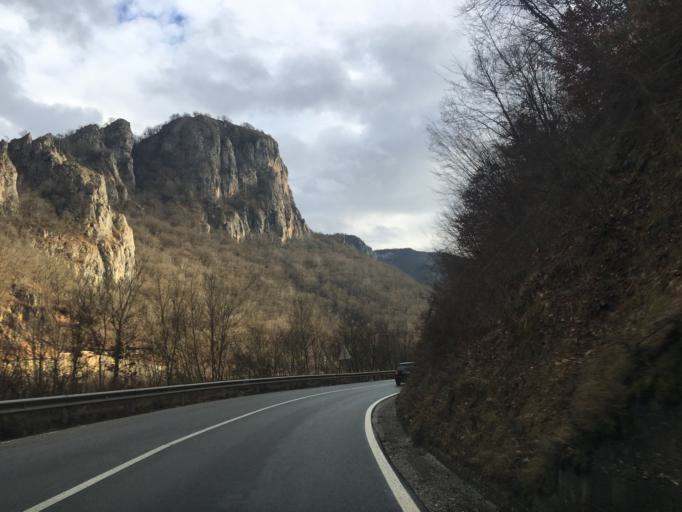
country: RS
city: Sokolovo Brdo
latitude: 43.1541
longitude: 19.7792
